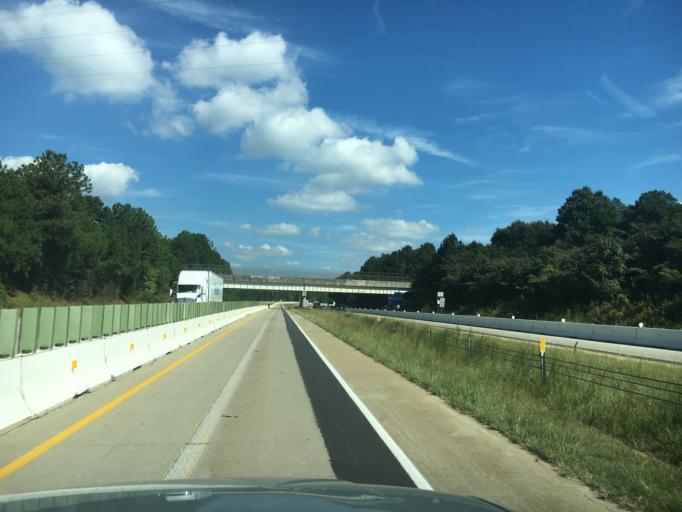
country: US
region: South Carolina
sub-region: Spartanburg County
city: Southern Shops
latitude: 34.9840
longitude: -82.0021
